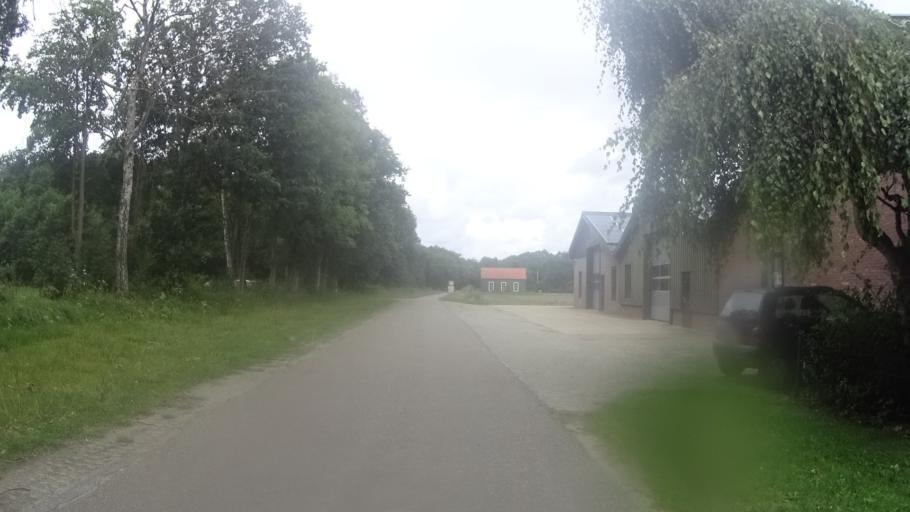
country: NL
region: North Holland
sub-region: Gemeente Castricum
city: Castricum
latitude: 52.5493
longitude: 4.6492
